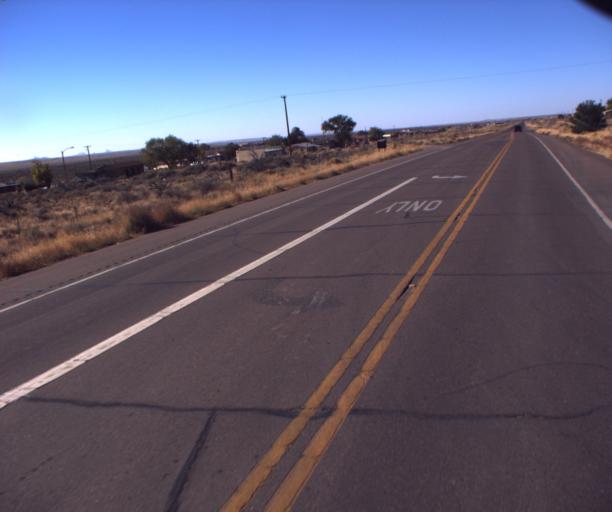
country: US
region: Arizona
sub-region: Navajo County
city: First Mesa
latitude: 35.8243
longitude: -110.3909
